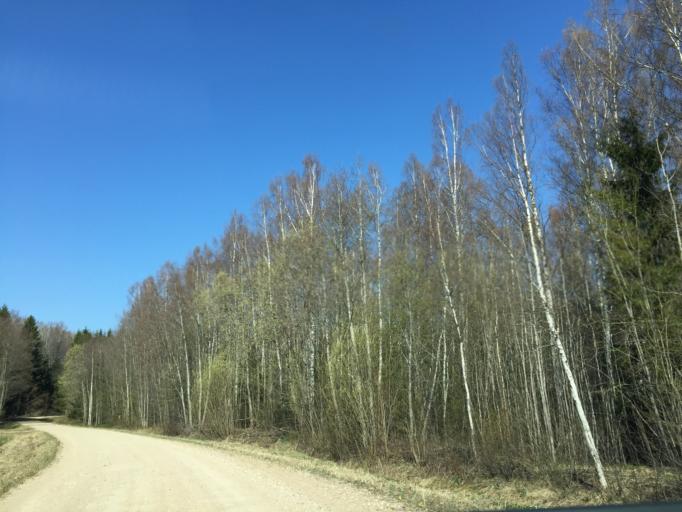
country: EE
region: Tartu
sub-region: Alatskivi vald
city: Kallaste
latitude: 58.5456
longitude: 26.9415
